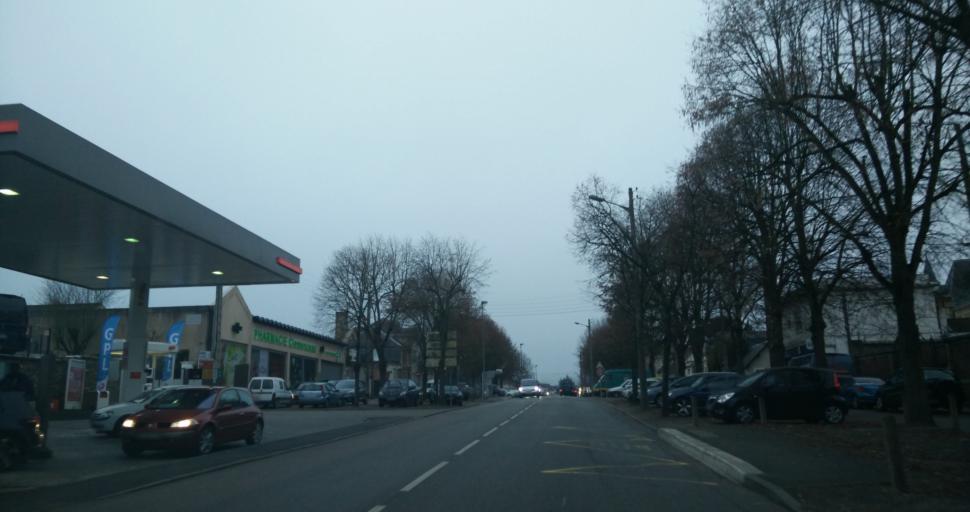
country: FR
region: Haute-Normandie
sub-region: Departement de l'Eure
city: Louviers
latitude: 49.2101
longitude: 1.1700
